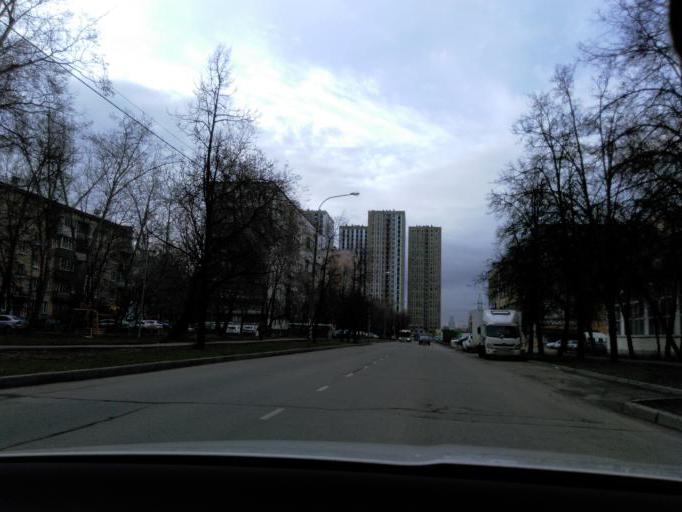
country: RU
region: Moskovskaya
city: Levoberezhnyy
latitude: 55.8444
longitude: 37.4907
